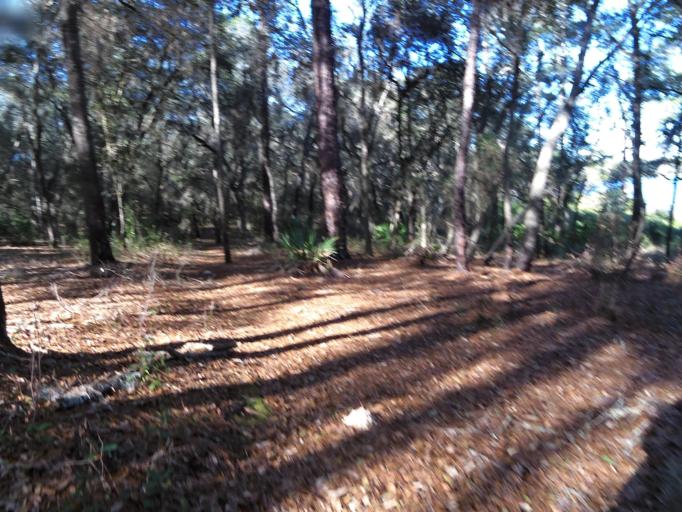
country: US
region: Florida
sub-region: Clay County
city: Keystone Heights
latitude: 29.8254
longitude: -82.0233
